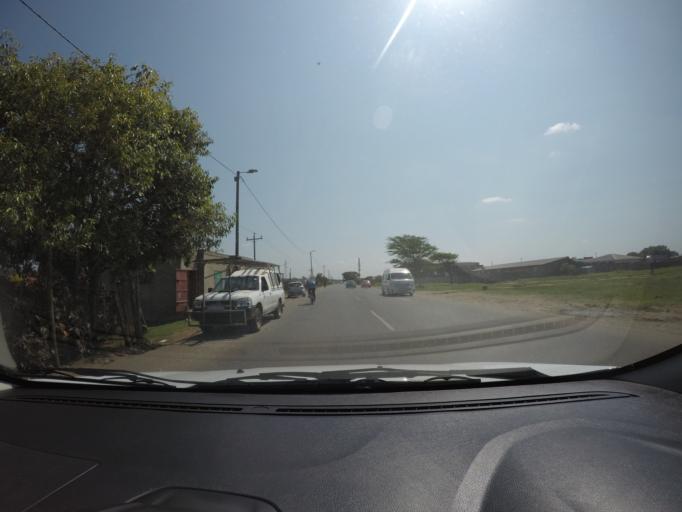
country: ZA
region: KwaZulu-Natal
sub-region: uThungulu District Municipality
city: eSikhawini
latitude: -28.8663
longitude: 31.9077
